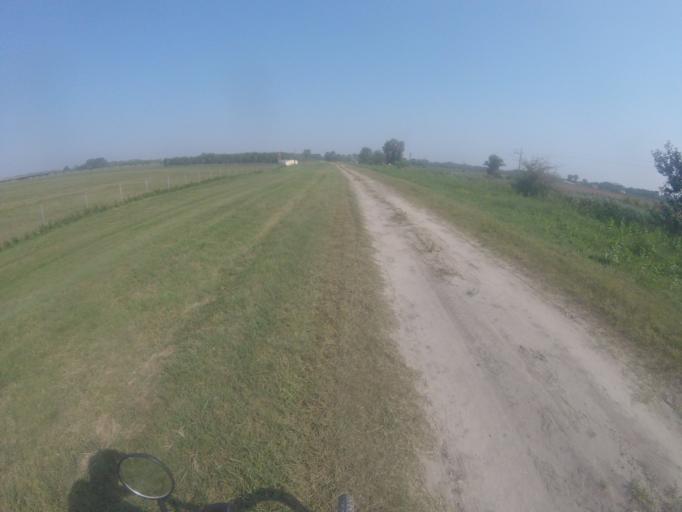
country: HU
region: Bacs-Kiskun
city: Ersekcsanad
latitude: 46.2307
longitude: 18.9621
